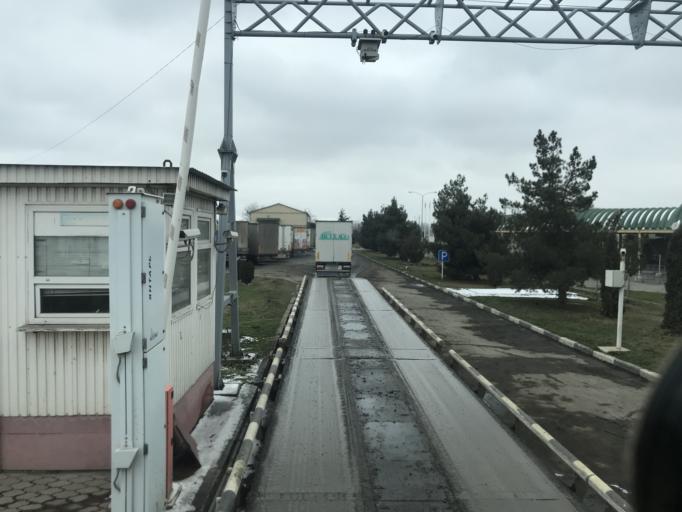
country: AZ
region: Qusar
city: Samur
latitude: 41.6403
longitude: 48.4080
